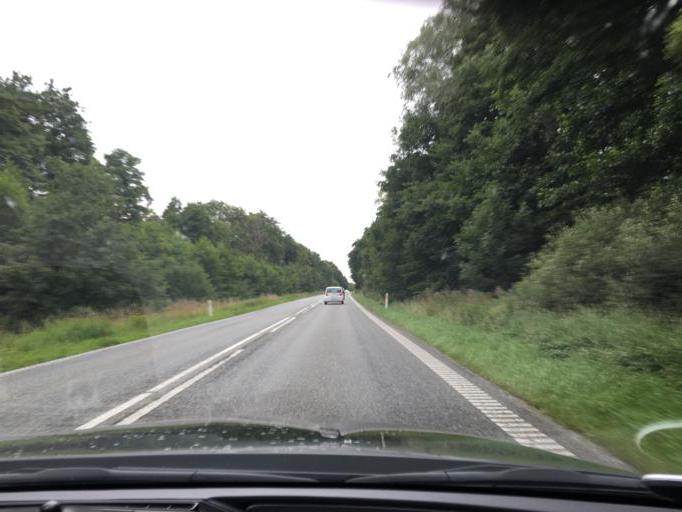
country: DK
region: Capital Region
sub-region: Allerod Kommune
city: Blovstrod
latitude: 55.9112
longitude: 12.3951
